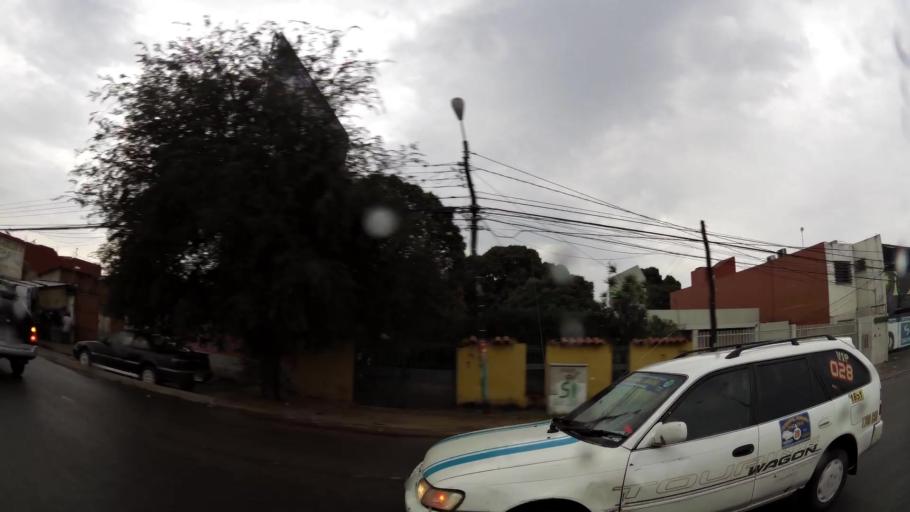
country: BO
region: Santa Cruz
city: Santa Cruz de la Sierra
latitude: -17.7767
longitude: -63.1390
